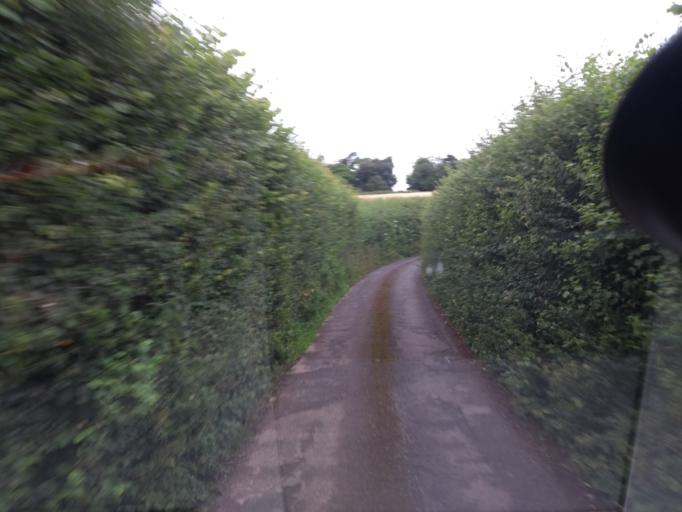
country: GB
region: England
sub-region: Somerset
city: North Petherton
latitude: 51.1333
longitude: -3.0901
